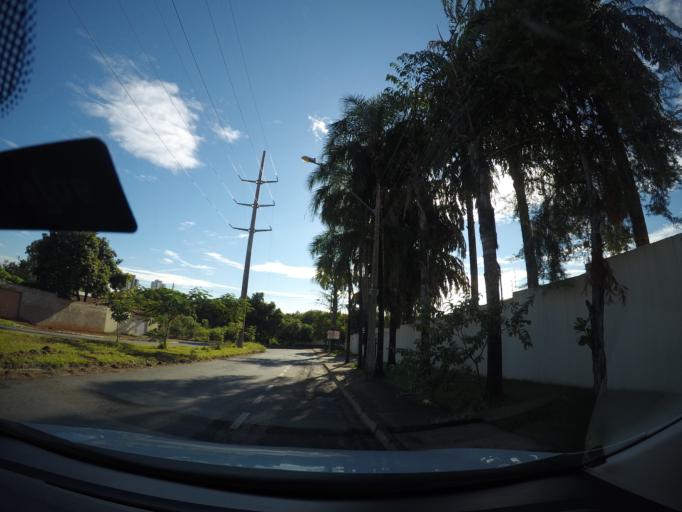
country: BR
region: Goias
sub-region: Goiania
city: Goiania
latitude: -16.7252
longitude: -49.2949
